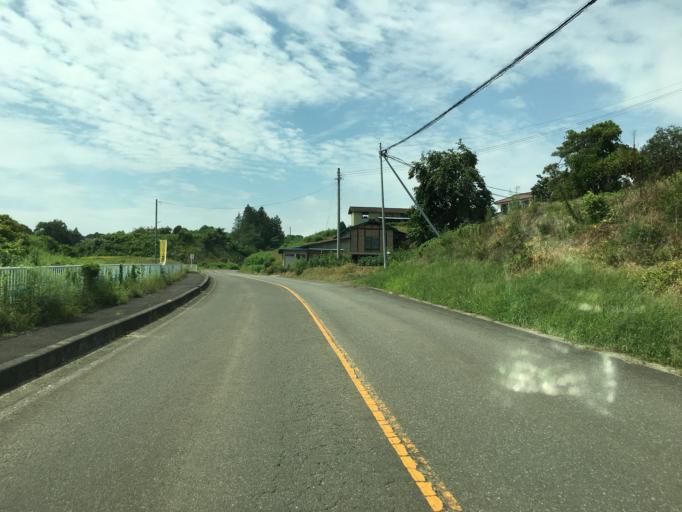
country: JP
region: Fukushima
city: Fukushima-shi
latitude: 37.6576
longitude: 140.5296
